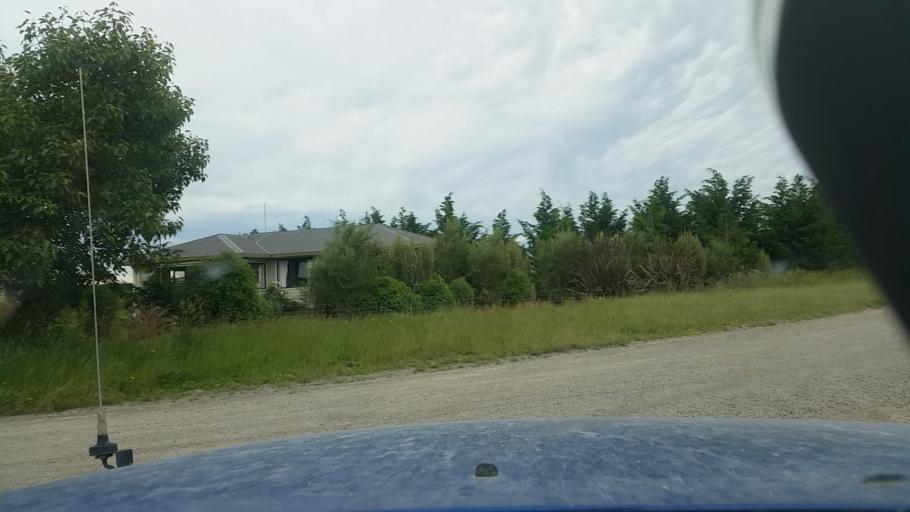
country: NZ
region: Canterbury
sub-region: Ashburton District
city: Tinwald
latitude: -43.8510
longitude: 171.5488
